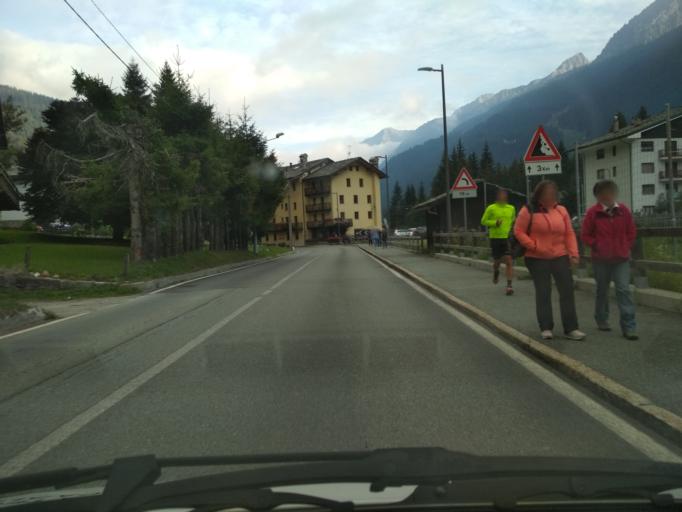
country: IT
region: Aosta Valley
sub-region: Valle d'Aosta
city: Gressoney-Saint-Jean
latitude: 45.7717
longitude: 7.8301
